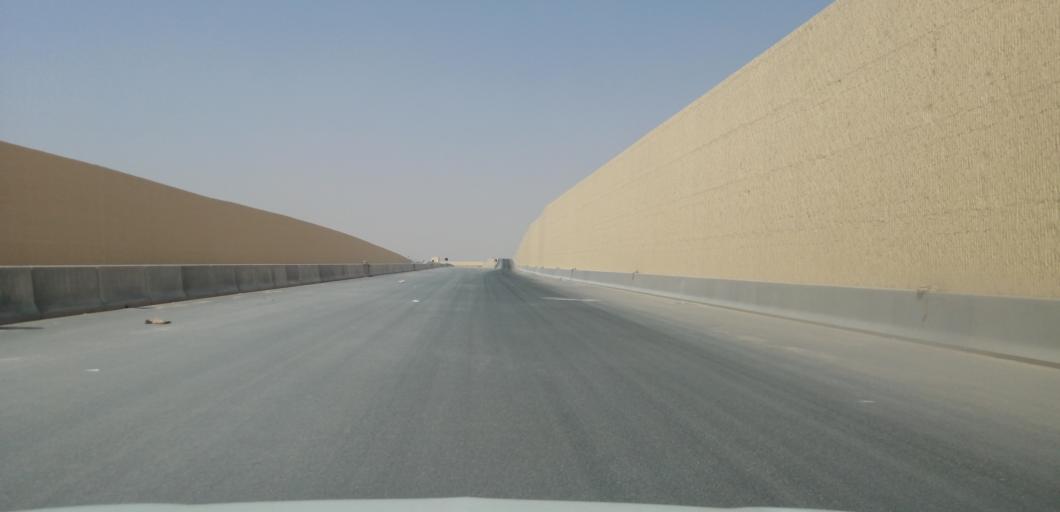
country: KW
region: Muhafazat al Jahra'
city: Al Jahra'
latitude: 29.4537
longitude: 47.5575
